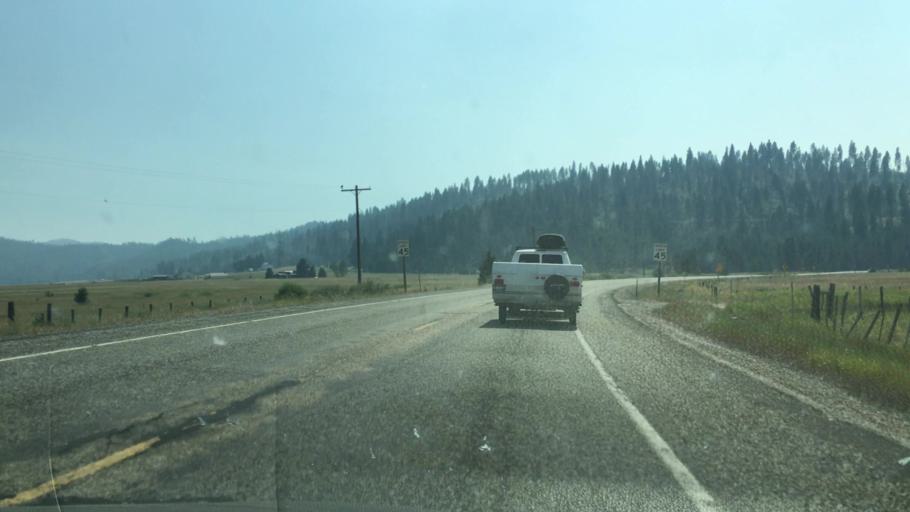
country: US
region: Idaho
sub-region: Valley County
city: Cascade
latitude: 44.3372
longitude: -116.0315
